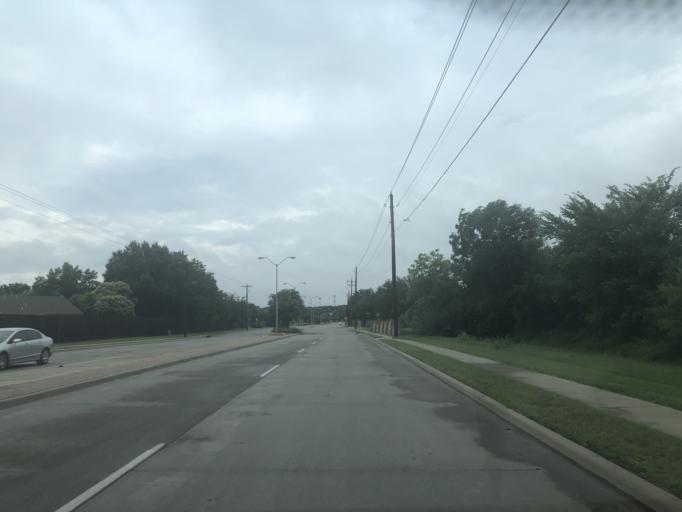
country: US
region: Texas
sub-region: Dallas County
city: Irving
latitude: 32.7894
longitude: -96.9596
